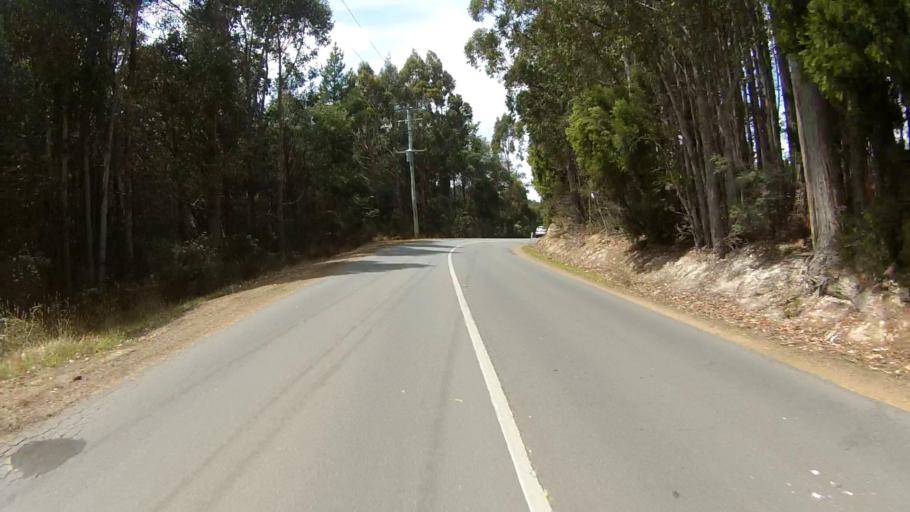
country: AU
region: Tasmania
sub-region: Kingborough
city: Kettering
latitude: -43.1052
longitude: 147.2394
